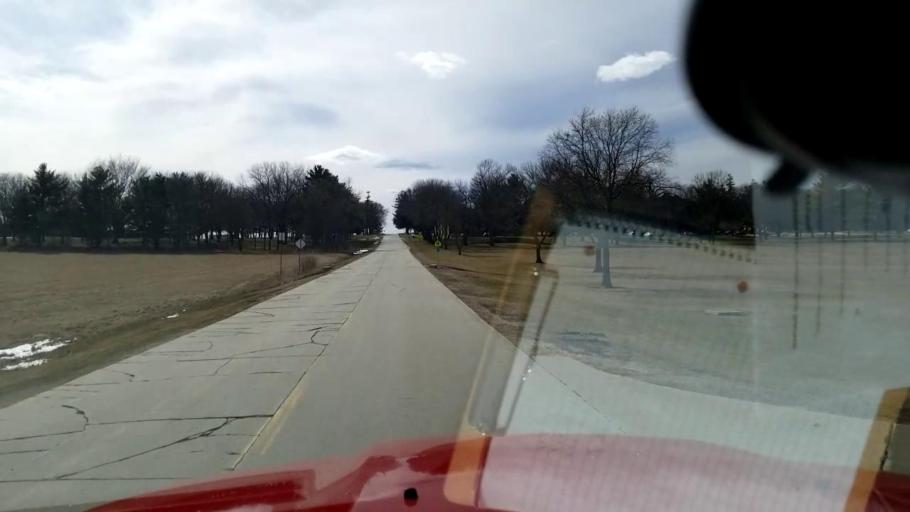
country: US
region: Iowa
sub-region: Buchanan County
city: Independence
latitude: 42.4542
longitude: -91.9215
